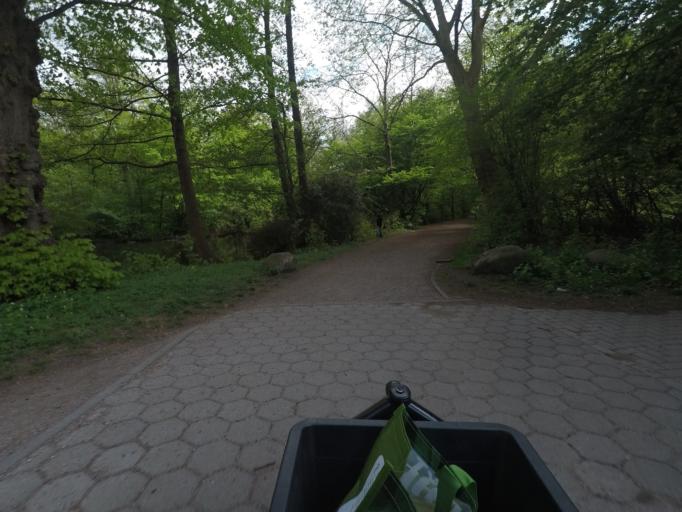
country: DE
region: Hamburg
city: Farmsen-Berne
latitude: 53.6266
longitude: 10.1337
